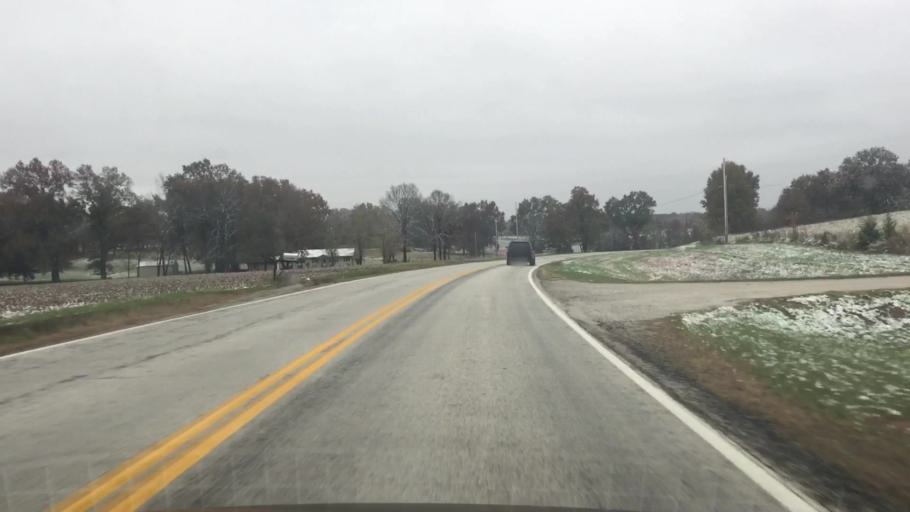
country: US
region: Missouri
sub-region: Saint Clair County
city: Osceola
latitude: 38.0362
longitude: -93.6862
